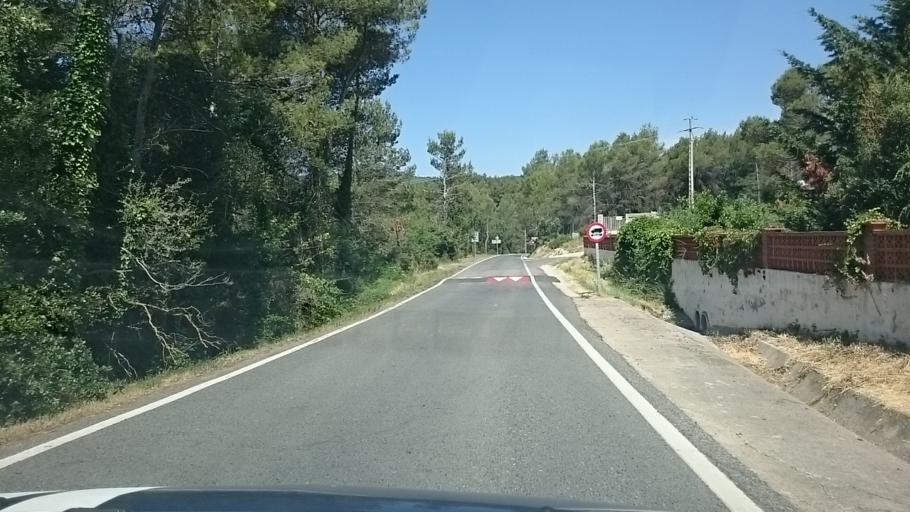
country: ES
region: Catalonia
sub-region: Provincia de Tarragona
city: Querol
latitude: 41.3962
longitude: 1.4548
